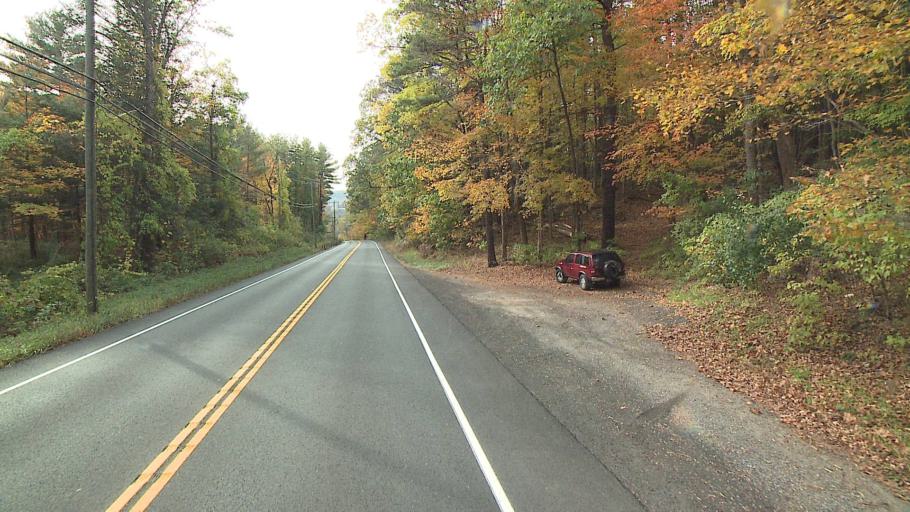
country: US
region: Connecticut
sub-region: Litchfield County
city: Canaan
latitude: 41.9997
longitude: -73.3973
